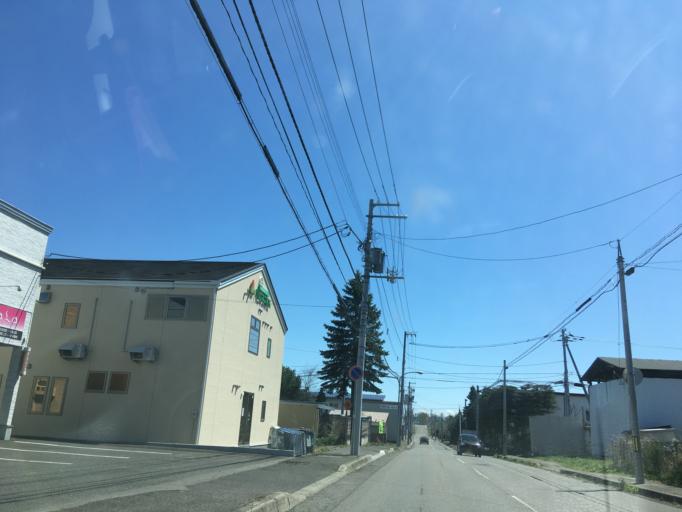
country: JP
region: Hokkaido
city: Obihiro
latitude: 42.9293
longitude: 143.1771
